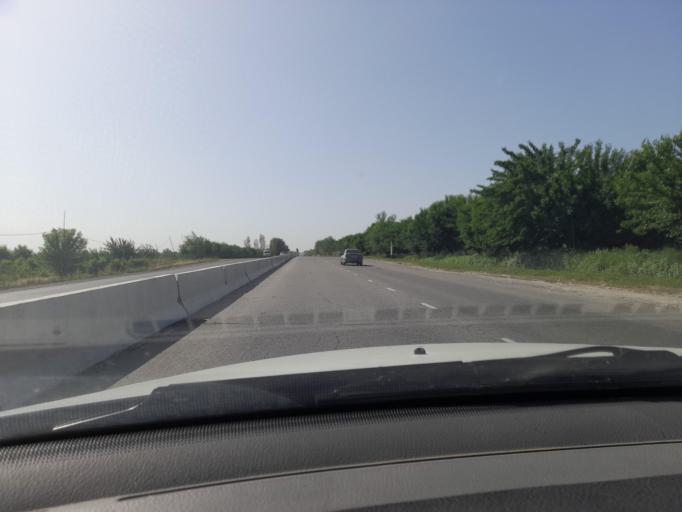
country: UZ
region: Samarqand
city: Chelak
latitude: 39.8442
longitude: 66.8127
